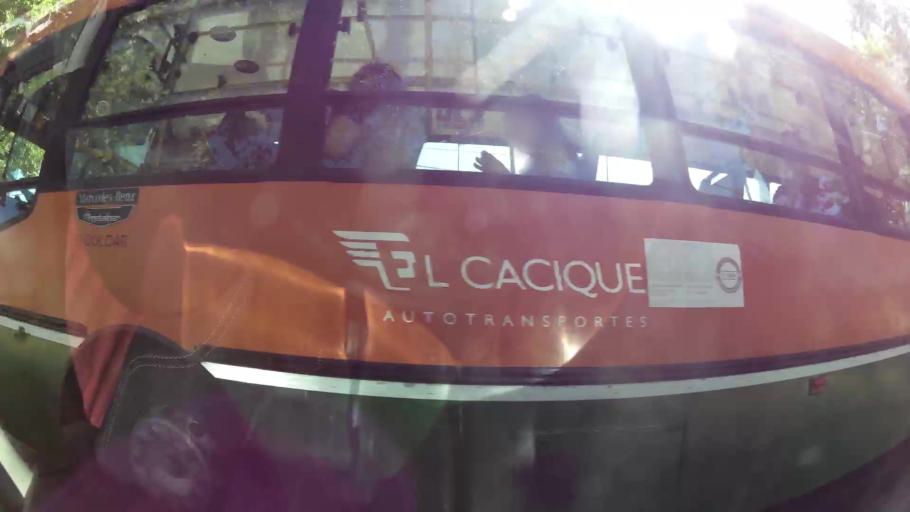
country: AR
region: Mendoza
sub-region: Departamento de Godoy Cruz
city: Godoy Cruz
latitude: -32.9427
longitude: -68.8210
